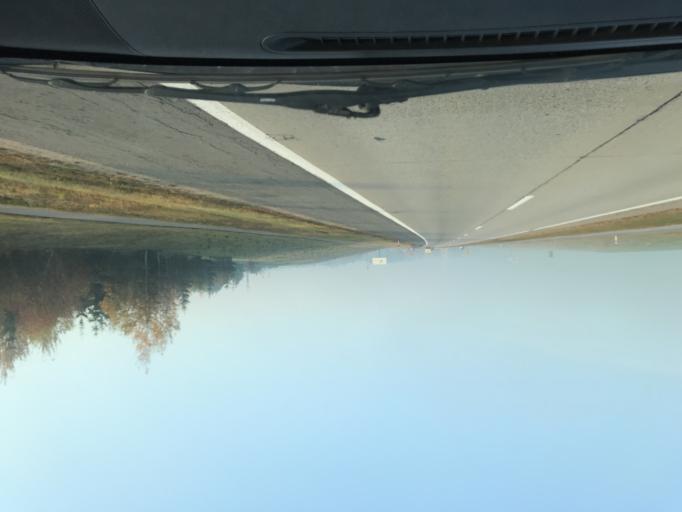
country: BY
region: Minsk
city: Borovlyany
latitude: 54.0098
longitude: 27.6584
